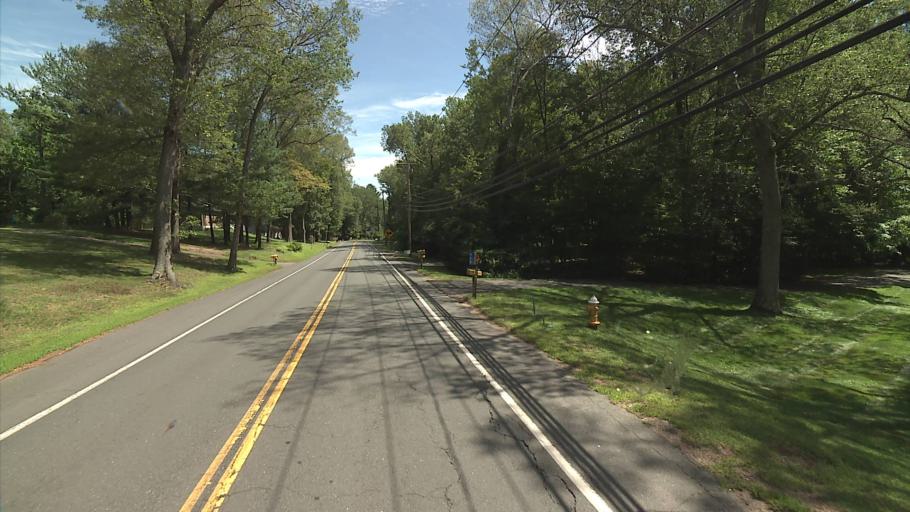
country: US
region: Connecticut
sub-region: Tolland County
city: Tolland
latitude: 41.8518
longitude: -72.3342
